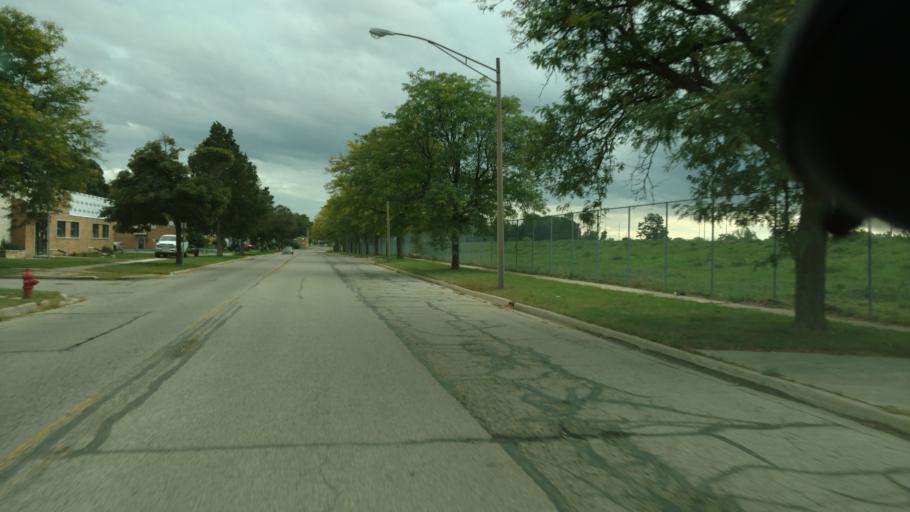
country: US
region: Michigan
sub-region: Ingham County
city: Edgemont Park
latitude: 42.7364
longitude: -84.5772
